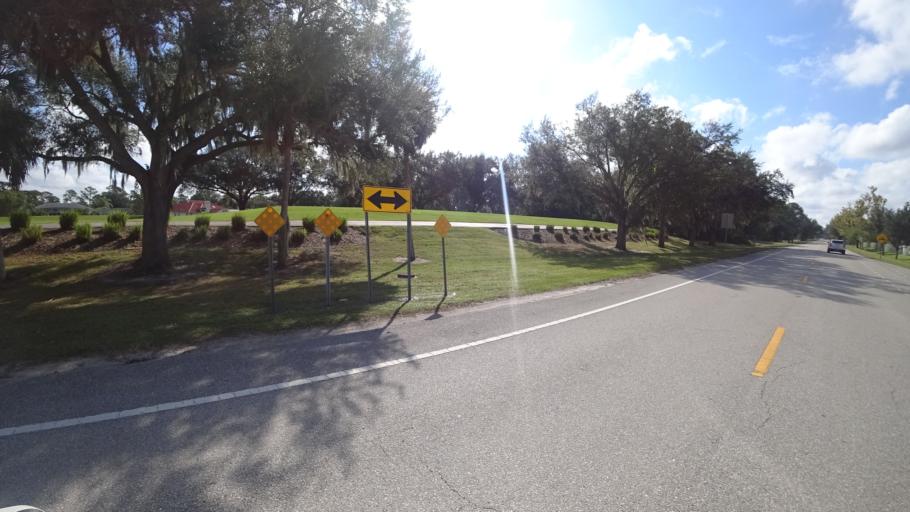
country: US
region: Florida
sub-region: Sarasota County
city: Desoto Lakes
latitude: 27.3994
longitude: -82.4872
